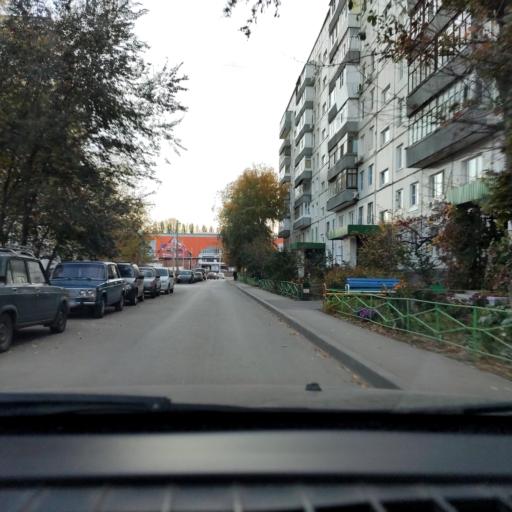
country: RU
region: Samara
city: Tol'yatti
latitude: 53.5087
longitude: 49.2672
